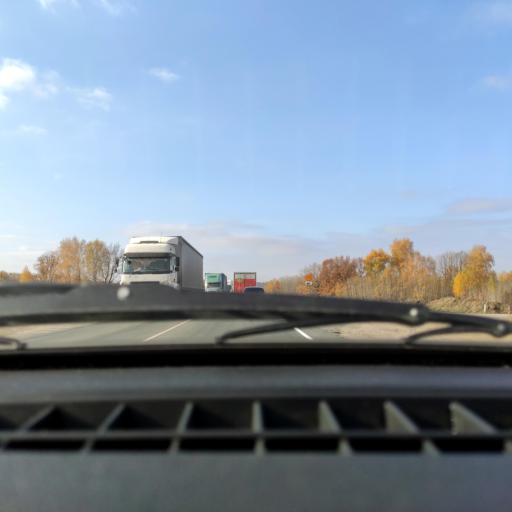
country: RU
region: Bashkortostan
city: Iglino
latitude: 54.7364
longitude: 56.2798
